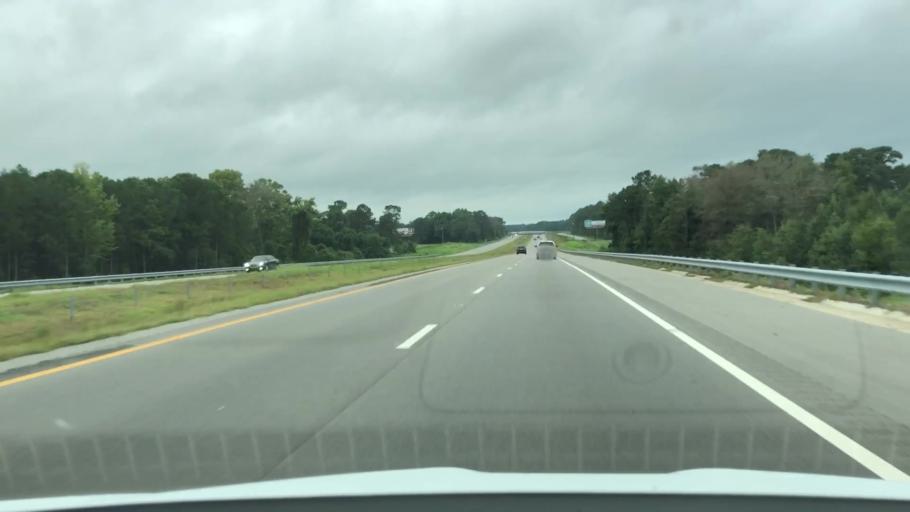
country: US
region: North Carolina
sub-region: Wayne County
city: Elroy
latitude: 35.3440
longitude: -77.8457
